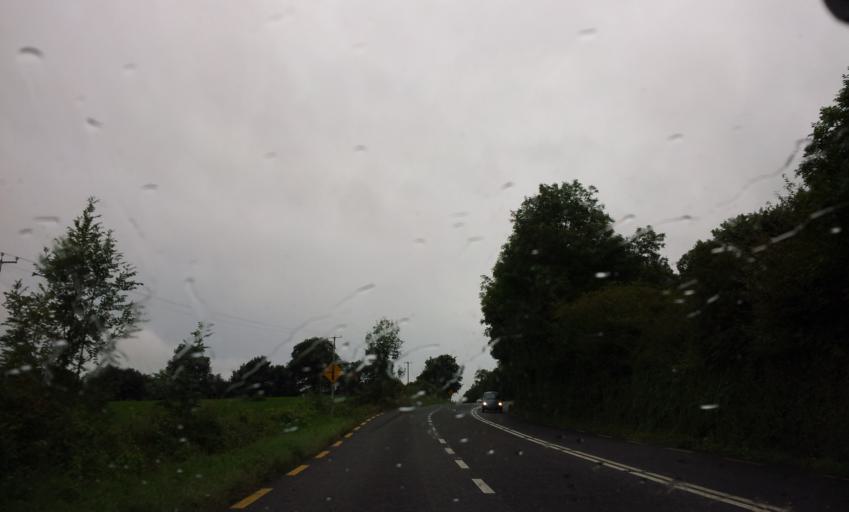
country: IE
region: Munster
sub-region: County Cork
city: Mitchelstown
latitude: 52.2422
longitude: -8.4551
